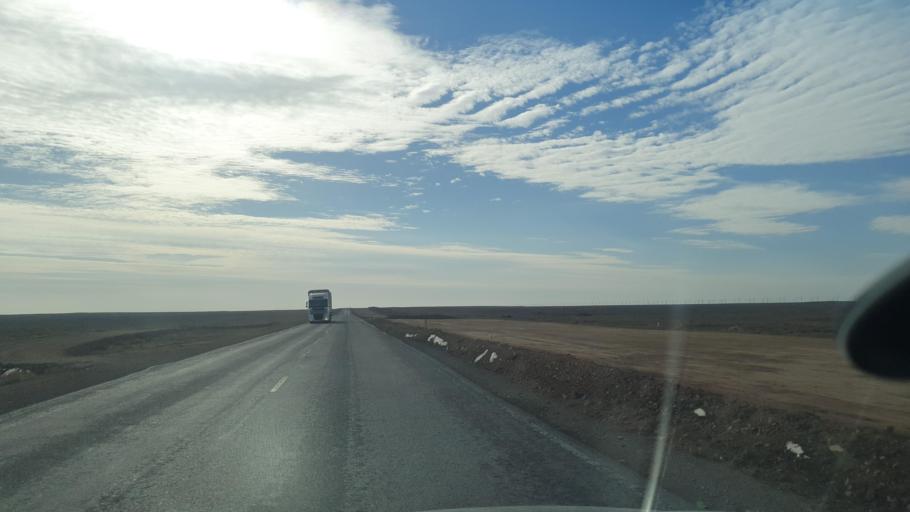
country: KZ
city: Priozersk
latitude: 45.9603
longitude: 73.5428
